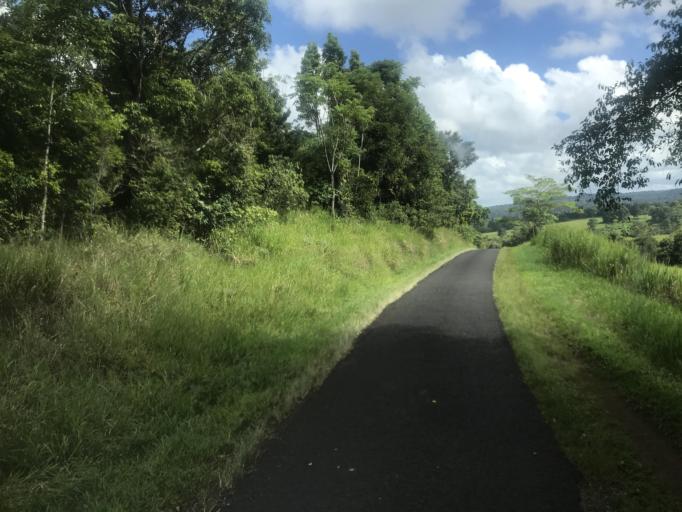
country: AU
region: Queensland
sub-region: Tablelands
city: Ravenshoe
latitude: -17.5419
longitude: 145.6917
